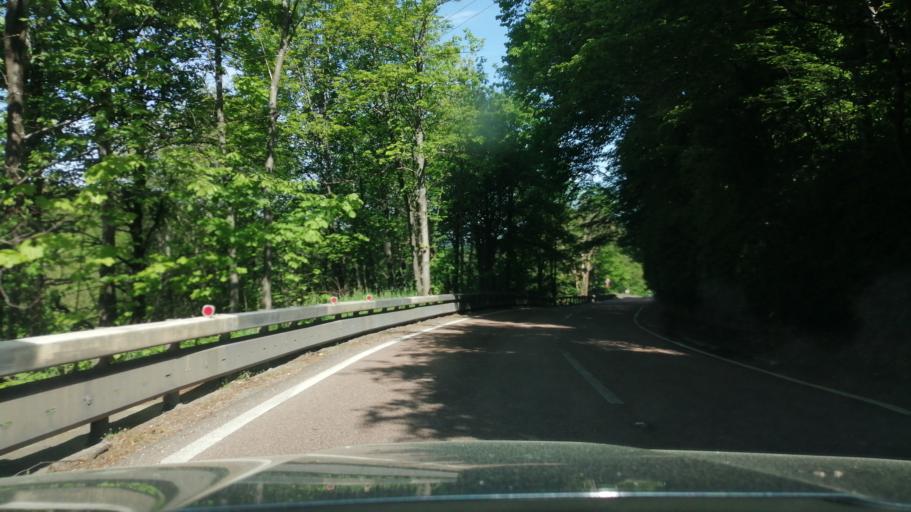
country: GB
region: Scotland
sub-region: Moray
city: Rothes
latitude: 57.4884
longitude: -3.1794
